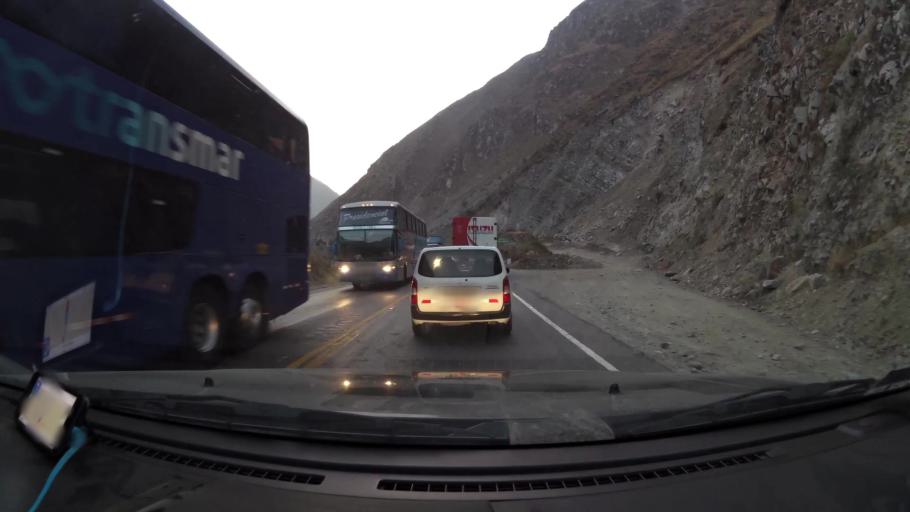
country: PE
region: Lima
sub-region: Provincia de Huarochiri
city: Surco
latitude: -11.8821
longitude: -76.4394
